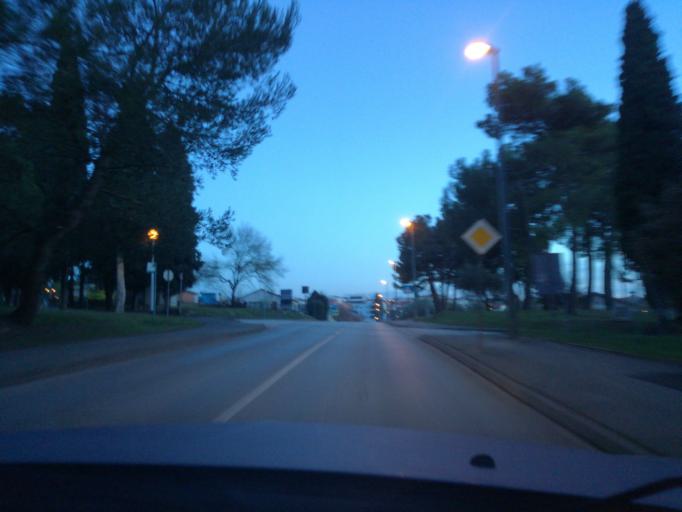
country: HR
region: Istarska
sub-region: Grad Rovinj
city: Rovinj
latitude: 45.0930
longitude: 13.6439
